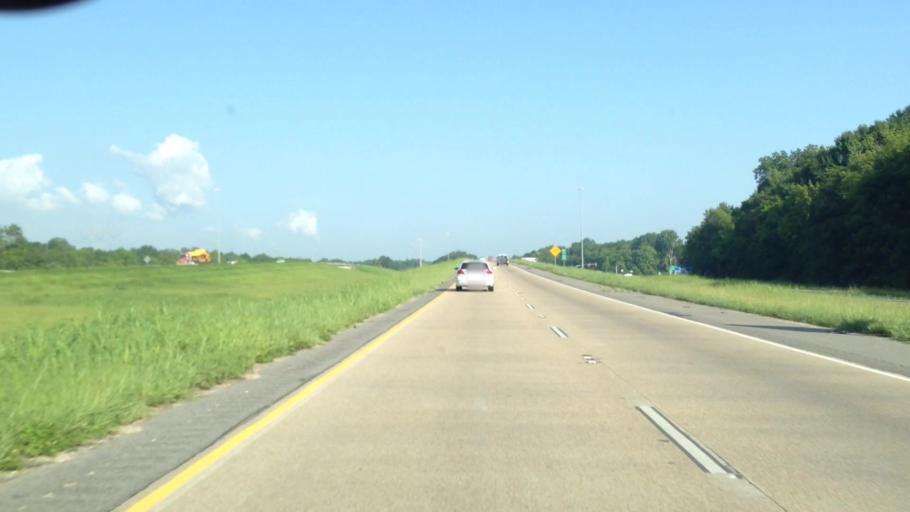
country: US
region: Louisiana
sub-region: Ascension Parish
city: Gonzales
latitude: 30.1908
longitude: -90.9162
